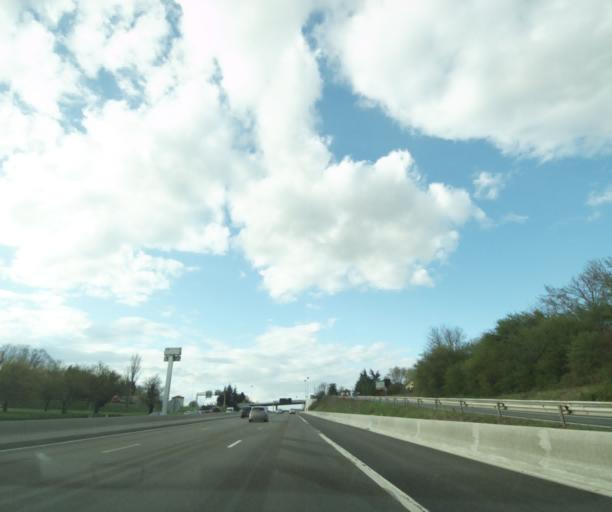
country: FR
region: Rhone-Alpes
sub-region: Departement du Rhone
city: Limonest
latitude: 45.8217
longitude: 4.7647
